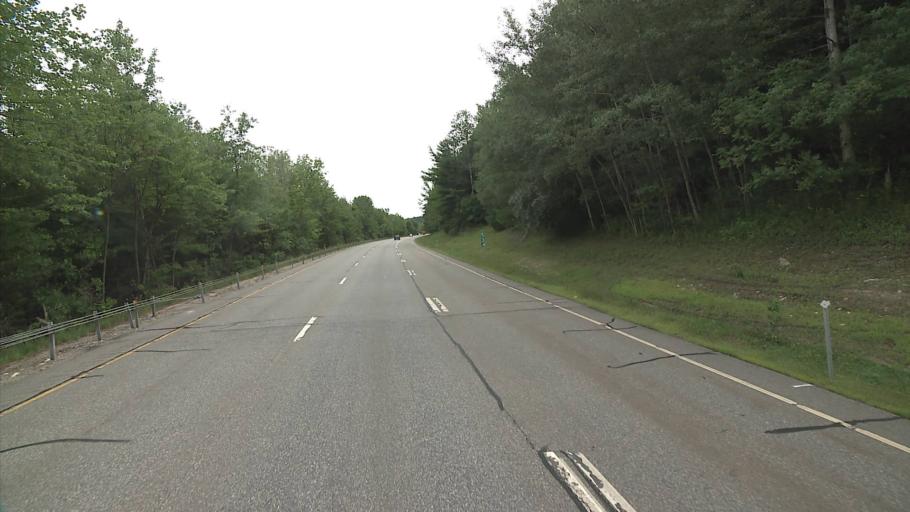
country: US
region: Connecticut
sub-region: Litchfield County
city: Torrington
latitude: 41.8500
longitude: -73.0925
